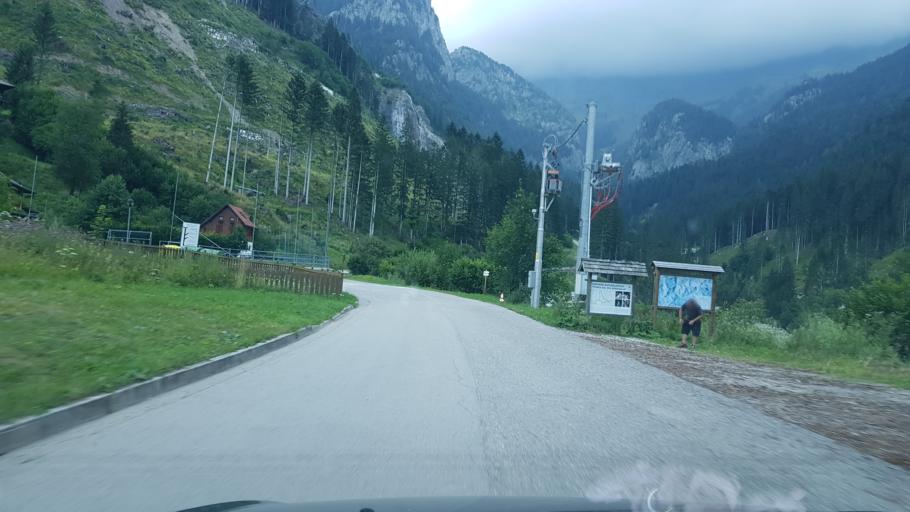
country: IT
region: Friuli Venezia Giulia
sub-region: Provincia di Udine
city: Forni Avoltri
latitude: 46.6096
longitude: 12.7788
